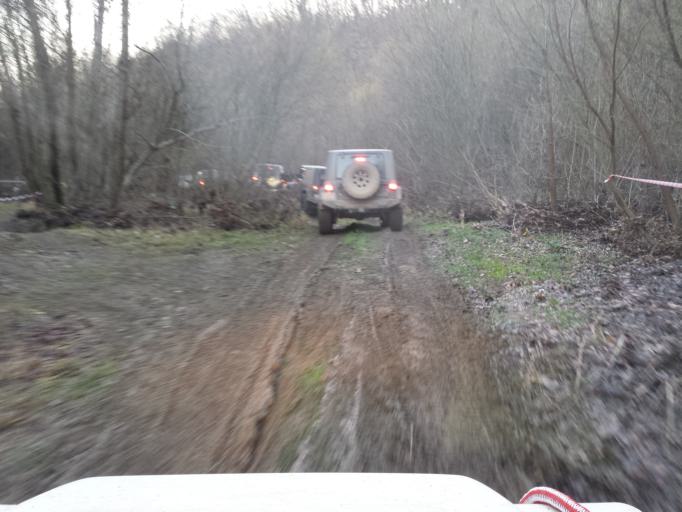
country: IT
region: Friuli Venezia Giulia
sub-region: Provincia di Udine
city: Corno di Rosazzo
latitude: 46.0046
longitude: 13.4606
